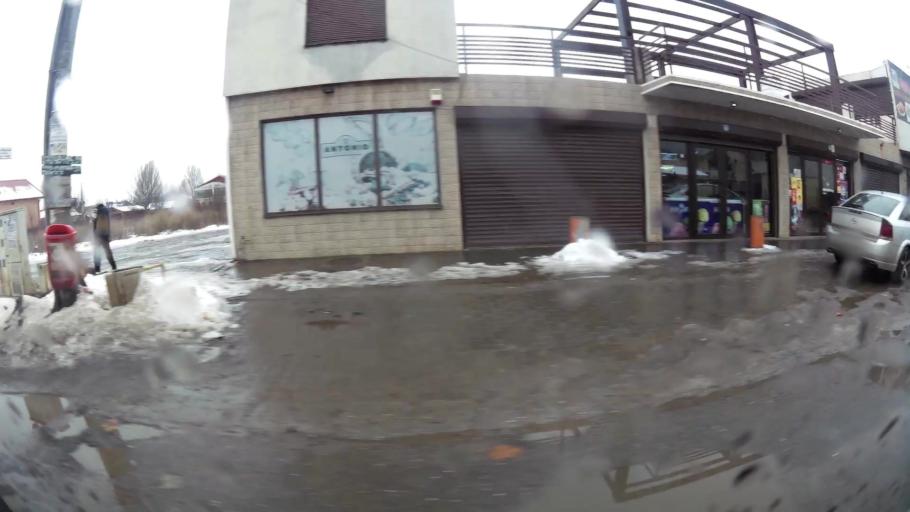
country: RO
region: Ilfov
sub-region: Comuna Bragadiru
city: Bragadiru
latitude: 44.3981
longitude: 26.0037
